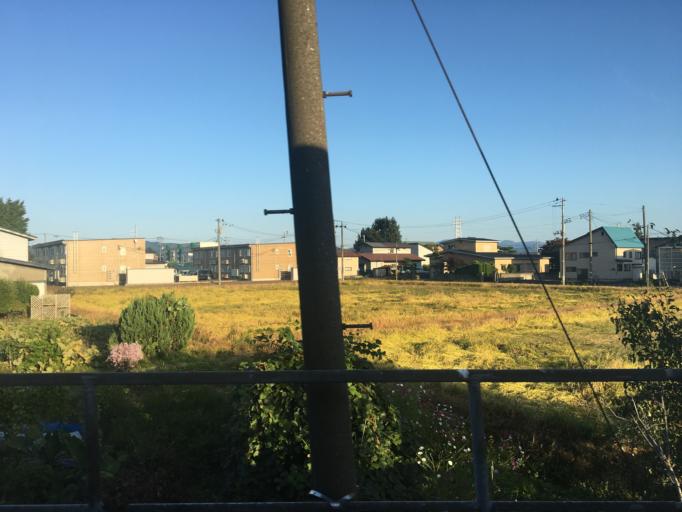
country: JP
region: Akita
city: Takanosu
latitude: 40.2244
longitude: 140.3577
